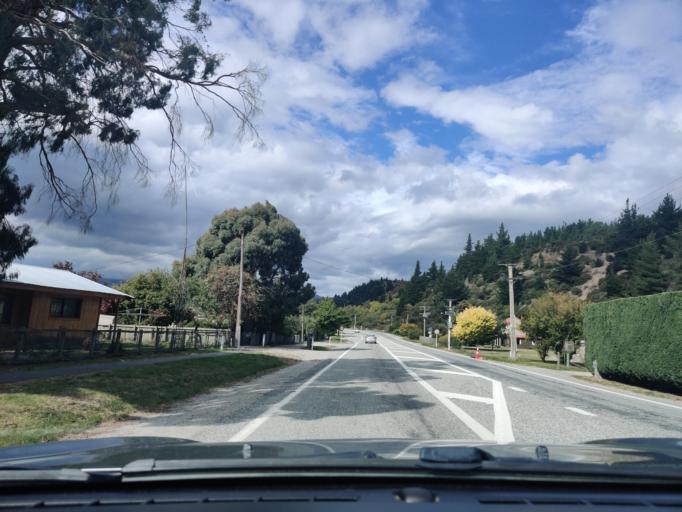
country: NZ
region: Otago
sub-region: Queenstown-Lakes District
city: Wanaka
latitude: -44.7497
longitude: 169.2711
